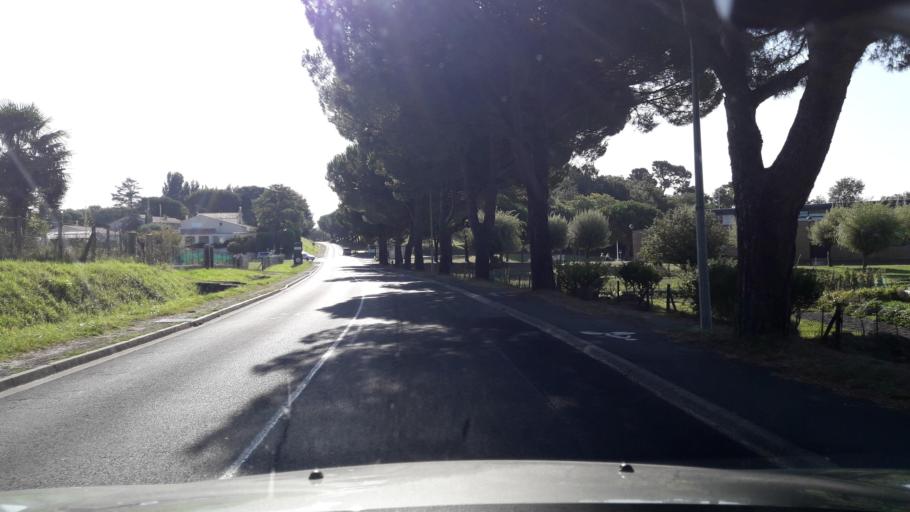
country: FR
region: Poitou-Charentes
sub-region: Departement de la Charente-Maritime
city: Les Mathes
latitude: 45.7155
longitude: -1.1492
